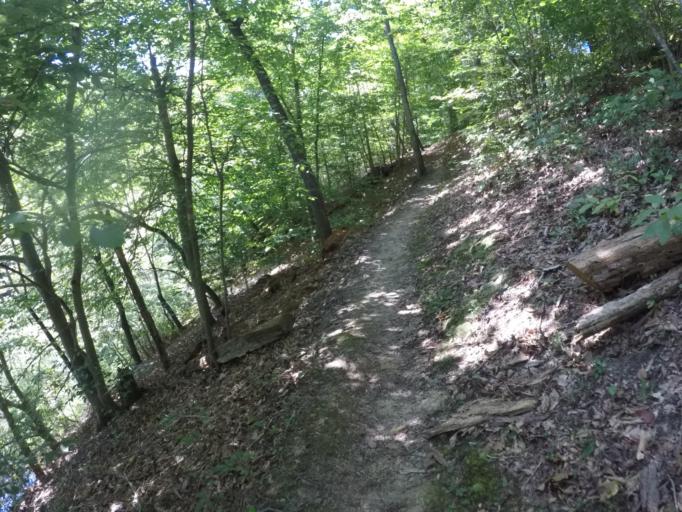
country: US
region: Ohio
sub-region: Lawrence County
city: Ironton
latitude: 38.6261
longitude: -82.6138
